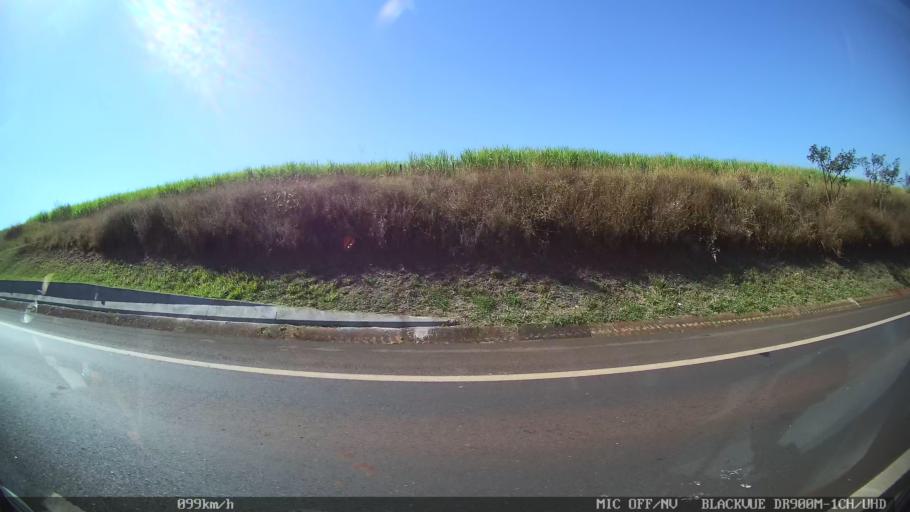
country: BR
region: Sao Paulo
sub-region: Batatais
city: Batatais
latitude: -20.8393
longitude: -47.6015
